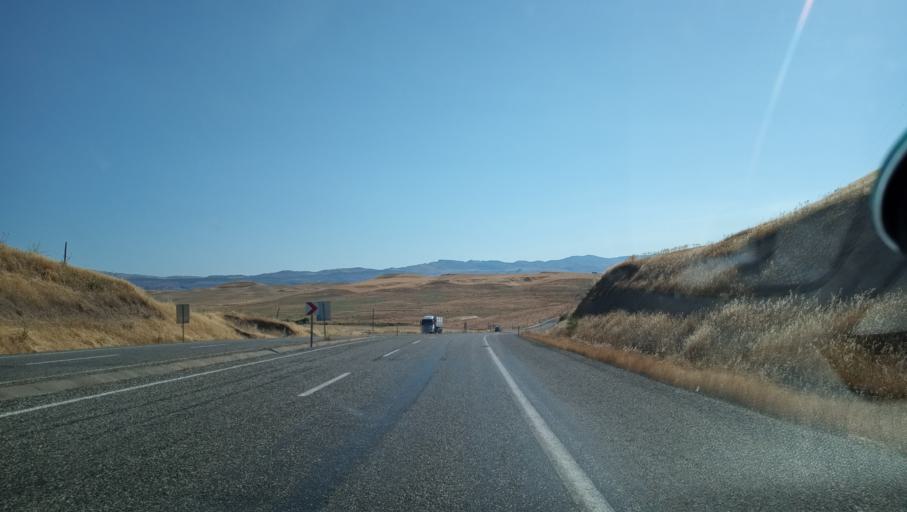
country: TR
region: Diyarbakir
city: Bagdere
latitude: 38.1242
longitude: 40.7450
